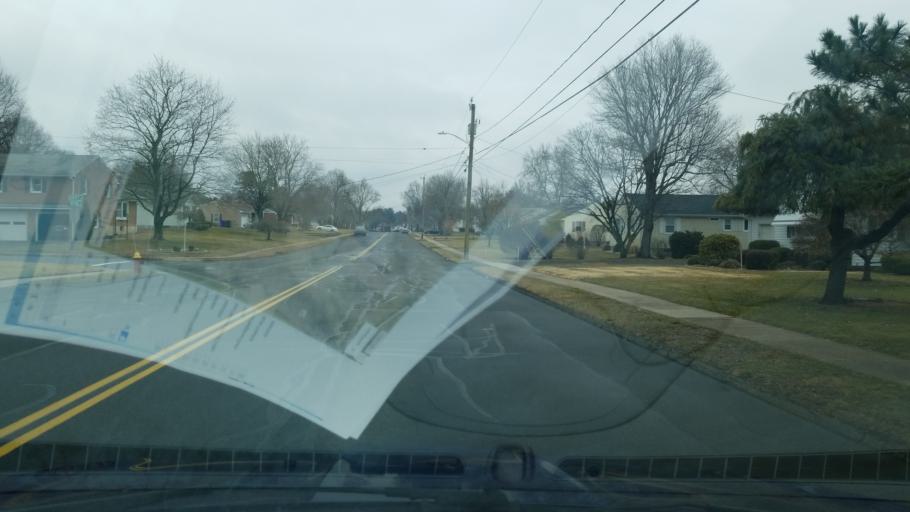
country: US
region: Connecticut
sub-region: Hartford County
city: Wethersfield
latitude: 41.6780
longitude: -72.6753
